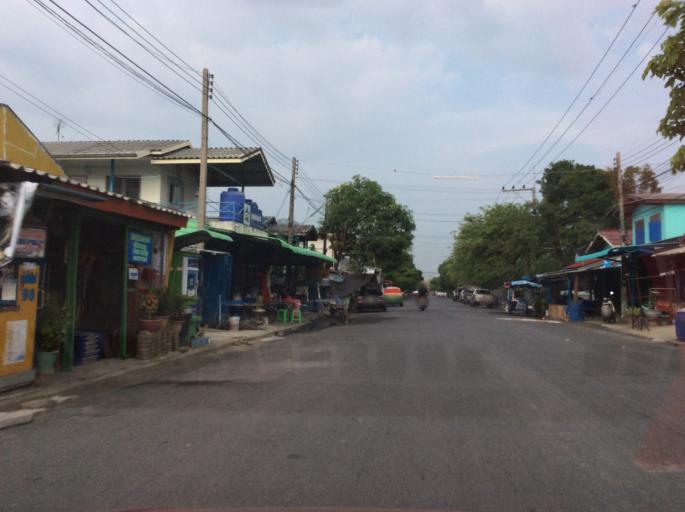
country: TH
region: Pathum Thani
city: Lam Luk Ka
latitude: 13.9484
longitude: 100.7328
